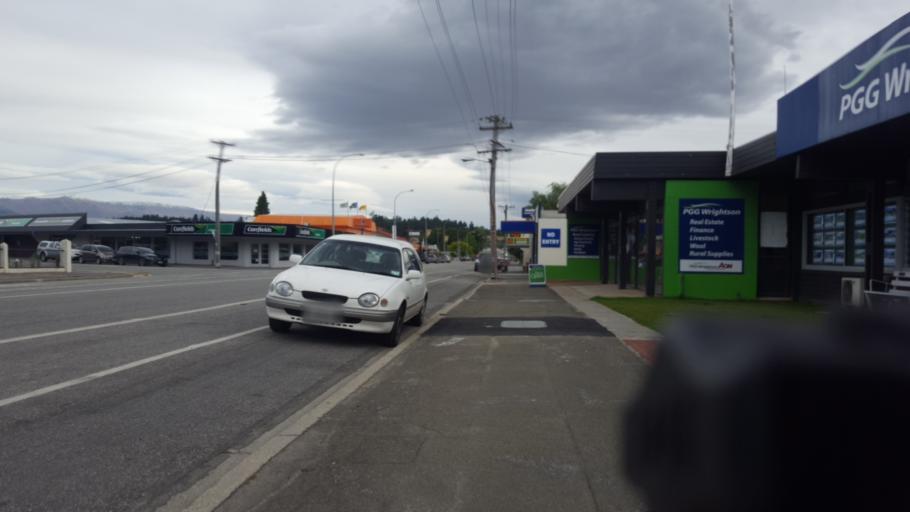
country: NZ
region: Otago
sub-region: Queenstown-Lakes District
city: Wanaka
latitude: -45.2538
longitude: 169.3944
